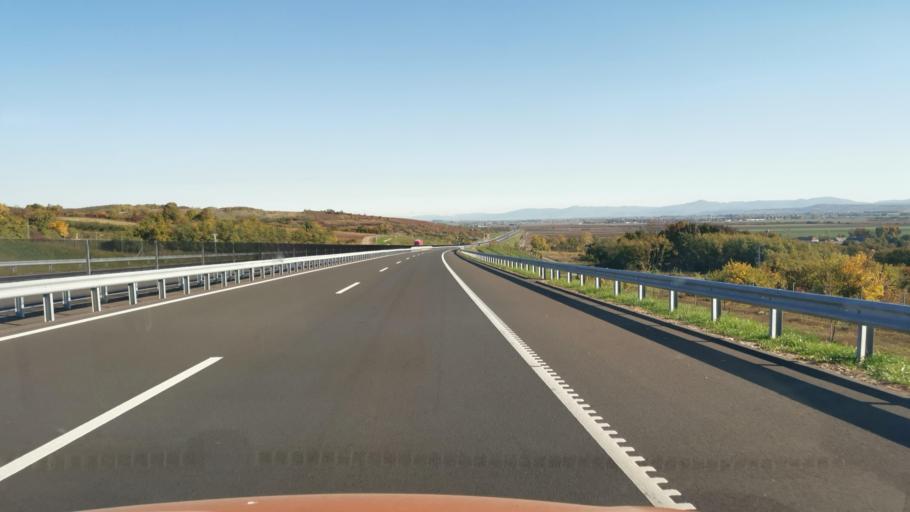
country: HU
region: Borsod-Abauj-Zemplen
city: Aszalo
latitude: 48.2249
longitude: 20.9420
